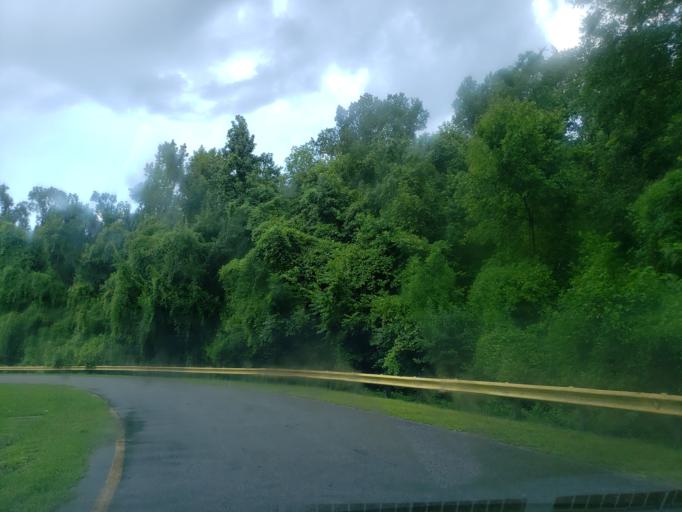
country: US
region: Georgia
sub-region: Chatham County
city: Thunderbolt
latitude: 32.0295
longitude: -81.0819
